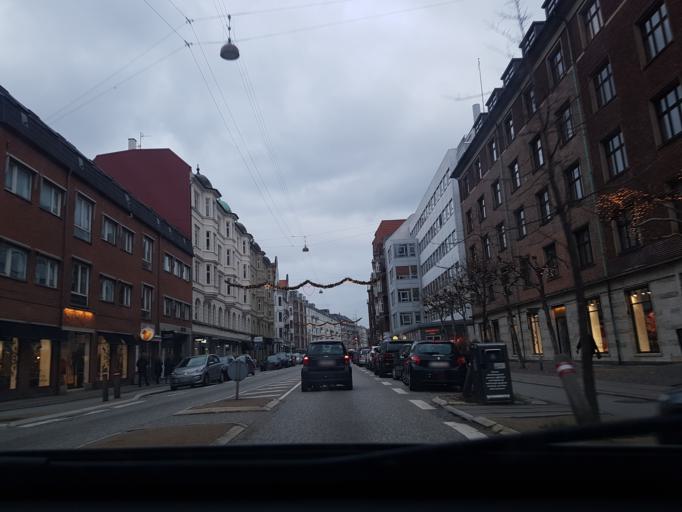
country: DK
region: Capital Region
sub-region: Gentofte Kommune
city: Charlottenlund
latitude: 55.7328
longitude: 12.5755
